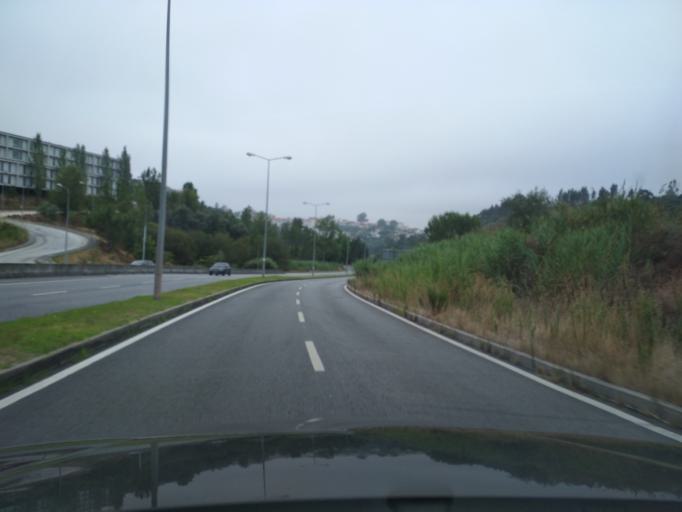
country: PT
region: Coimbra
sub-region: Coimbra
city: Coimbra
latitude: 40.2216
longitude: -8.4168
